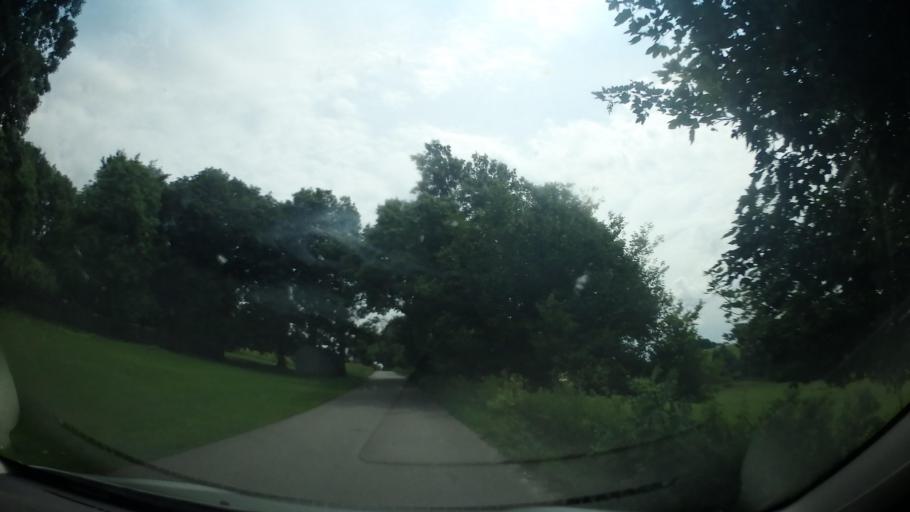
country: CZ
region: Vysocina
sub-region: Okres Zd'ar nad Sazavou
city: Nove Mesto na Morave
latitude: 49.5995
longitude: 16.0623
